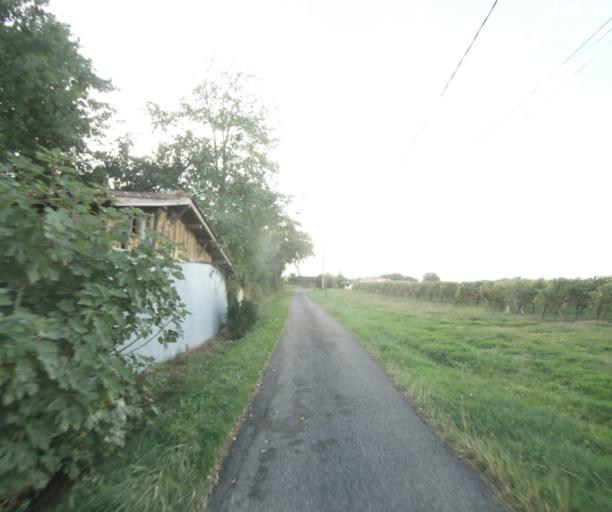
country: FR
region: Midi-Pyrenees
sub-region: Departement du Gers
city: Le Houga
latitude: 43.8388
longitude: -0.1251
